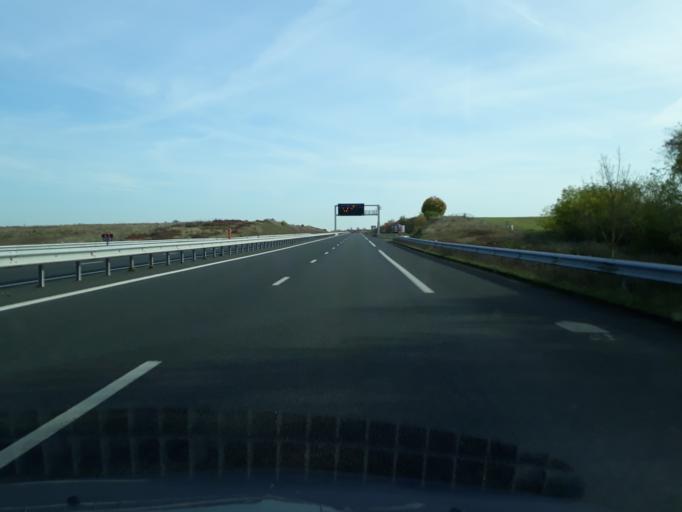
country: FR
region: Champagne-Ardenne
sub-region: Departement de l'Aube
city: Bucheres
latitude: 48.2234
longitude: 4.0939
